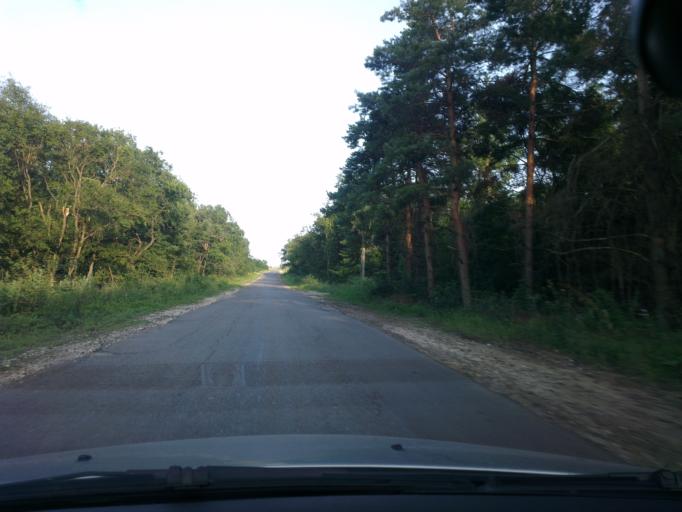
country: MD
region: Cantemir
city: Iargara
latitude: 46.3682
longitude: 28.3853
